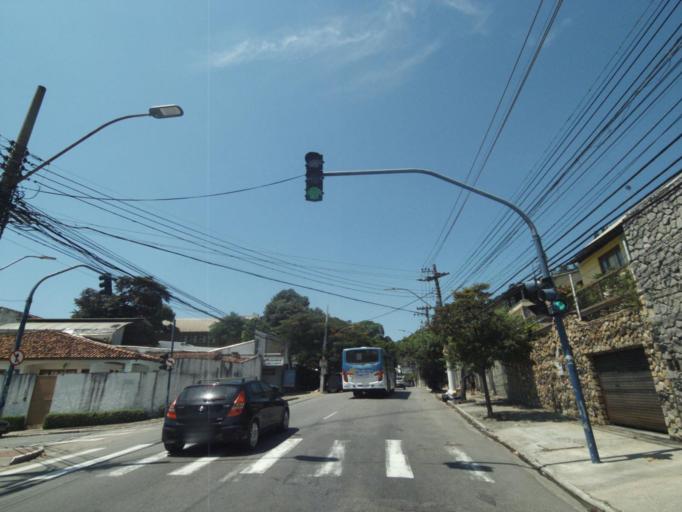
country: BR
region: Rio de Janeiro
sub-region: Niteroi
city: Niteroi
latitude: -22.9131
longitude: -43.0802
